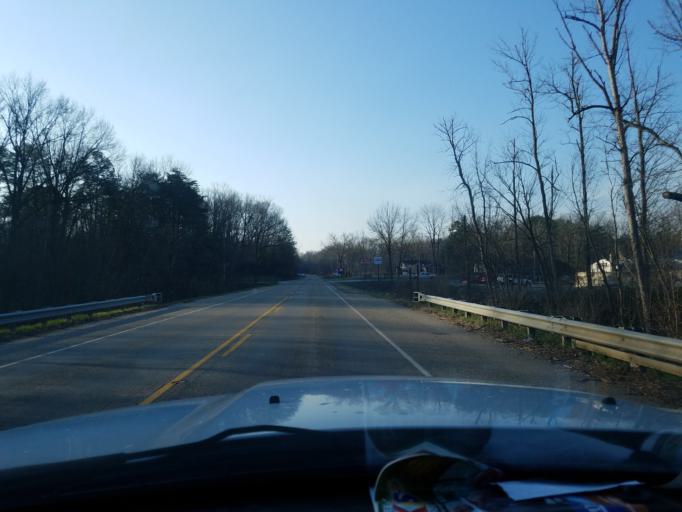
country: US
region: Indiana
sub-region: Vigo County
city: Seelyville
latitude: 39.4035
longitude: -87.3207
